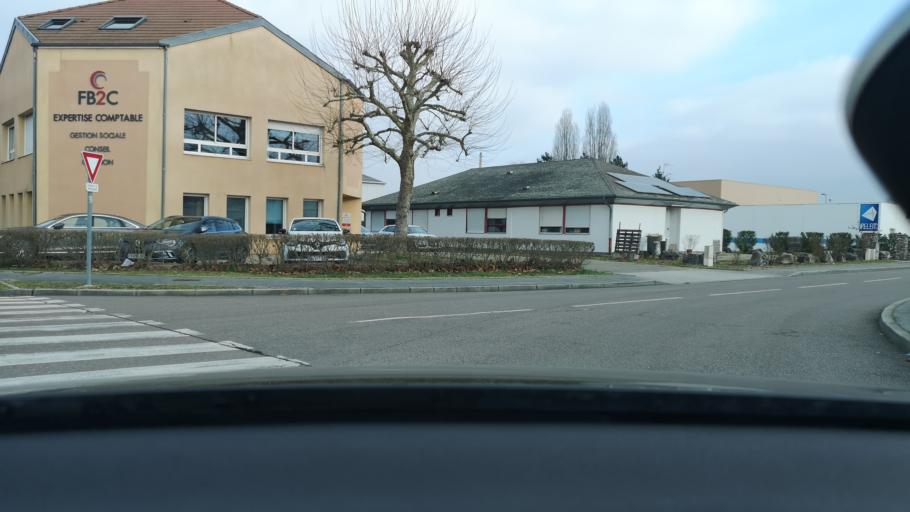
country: FR
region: Bourgogne
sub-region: Departement de Saone-et-Loire
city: Chatenoy-le-Royal
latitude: 46.7948
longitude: 4.8290
